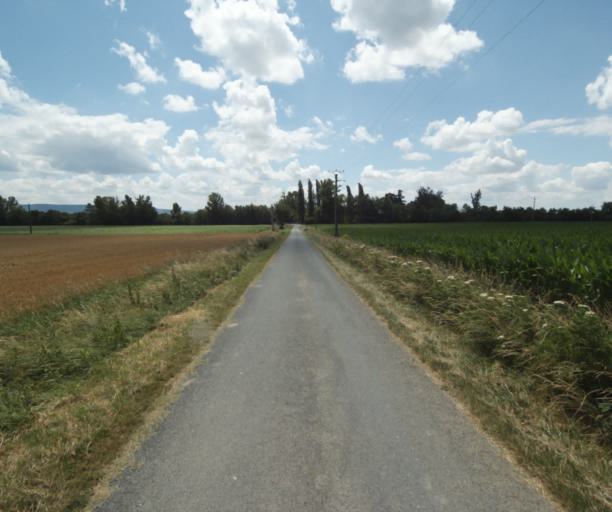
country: FR
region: Midi-Pyrenees
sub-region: Departement du Tarn
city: Puylaurens
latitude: 43.5224
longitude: 2.0237
